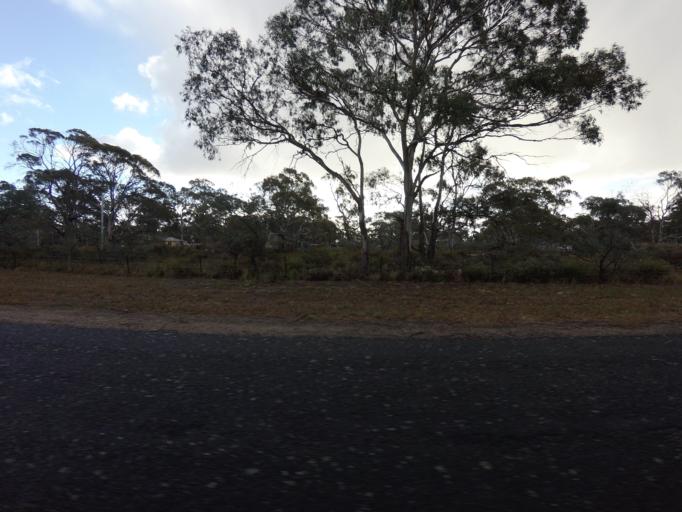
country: AU
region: Tasmania
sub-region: Break O'Day
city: St Helens
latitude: -42.1071
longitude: 148.0748
